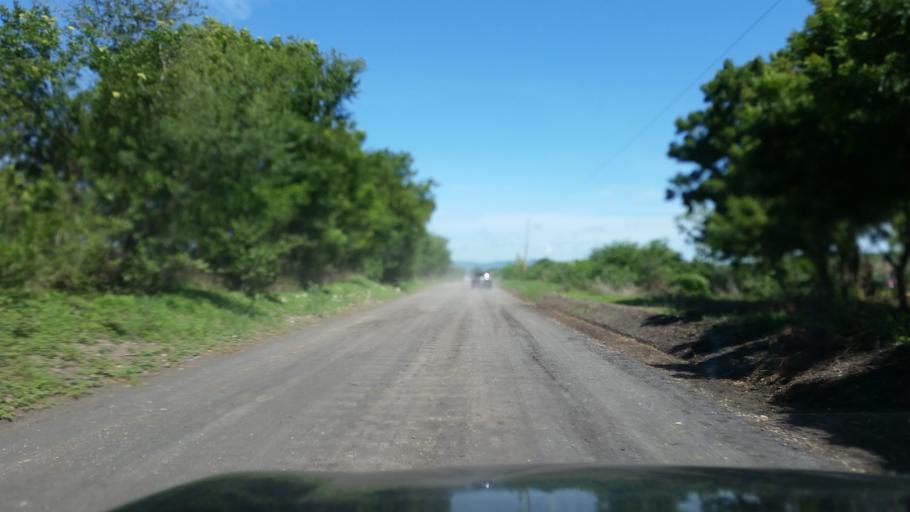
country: NI
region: Chinandega
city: Puerto Morazan
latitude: 12.7707
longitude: -87.0843
